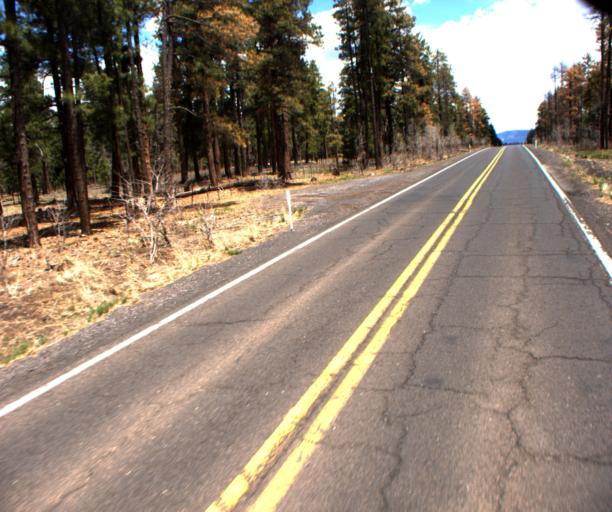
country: US
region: Arizona
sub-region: Coconino County
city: Kachina Village
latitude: 35.1119
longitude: -111.7147
